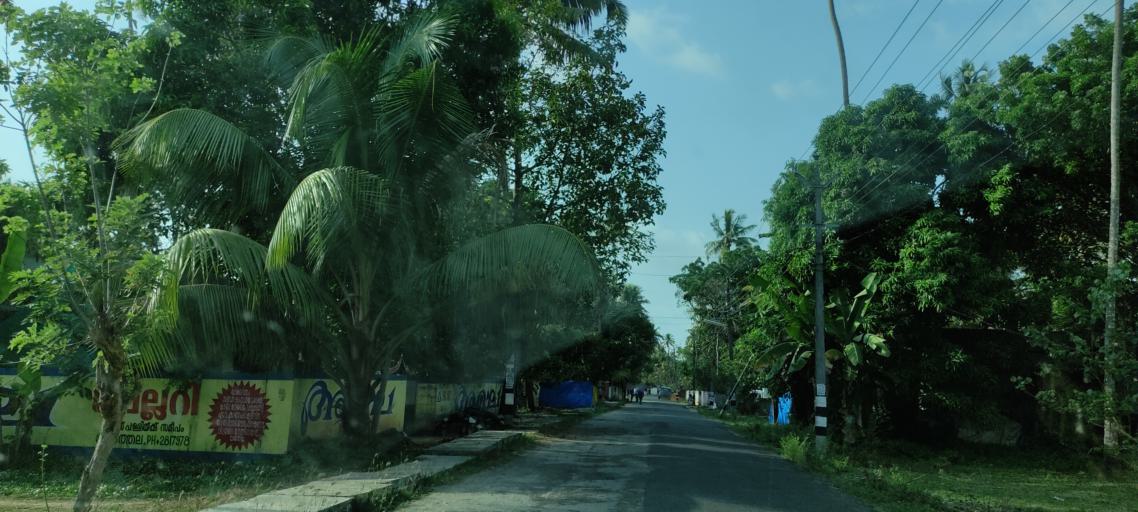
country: IN
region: Kerala
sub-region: Alappuzha
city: Vayalar
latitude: 9.7191
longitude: 76.2875
